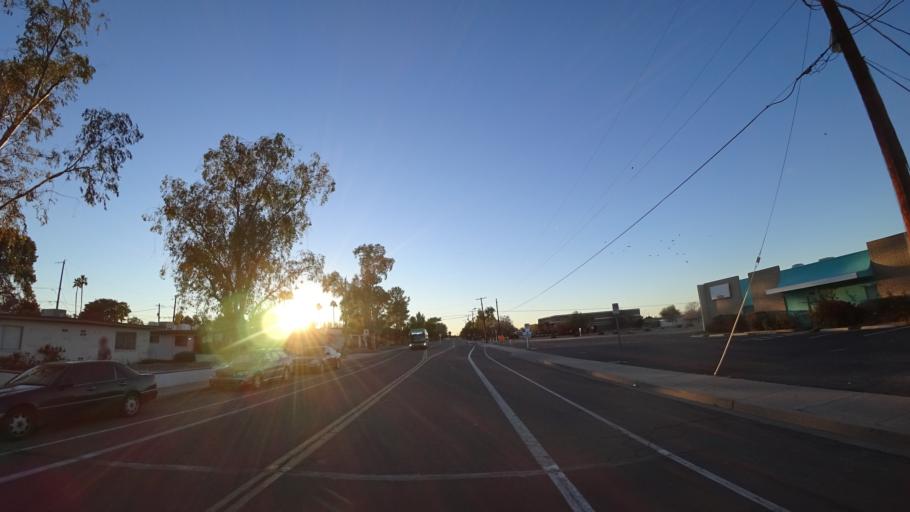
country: US
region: Arizona
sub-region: Maricopa County
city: Tempe Junction
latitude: 33.4291
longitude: -111.9513
